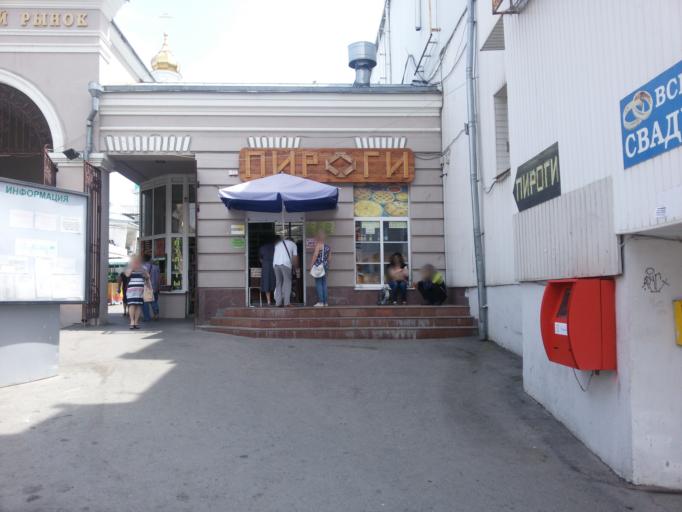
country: RU
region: Rostov
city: Rostov-na-Donu
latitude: 47.2164
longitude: 39.7095
